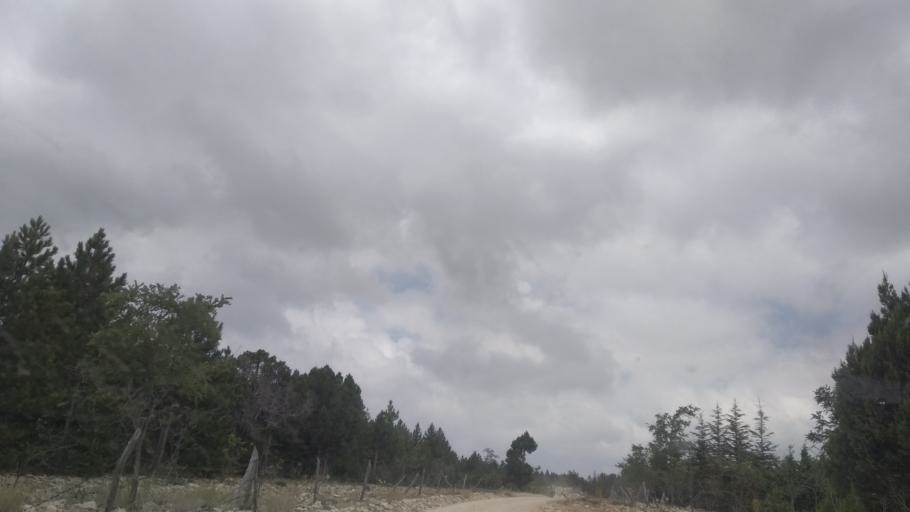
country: TR
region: Mersin
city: Sarikavak
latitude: 36.5724
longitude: 33.7619
